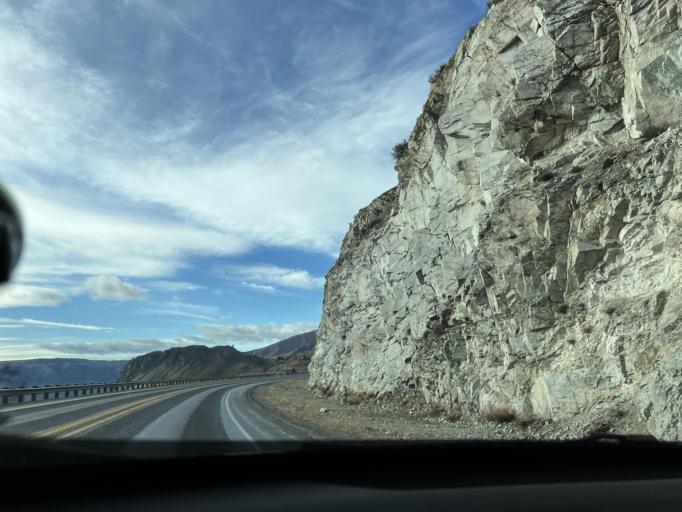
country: US
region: Washington
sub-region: Chelan County
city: Chelan
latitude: 47.8563
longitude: -119.9582
